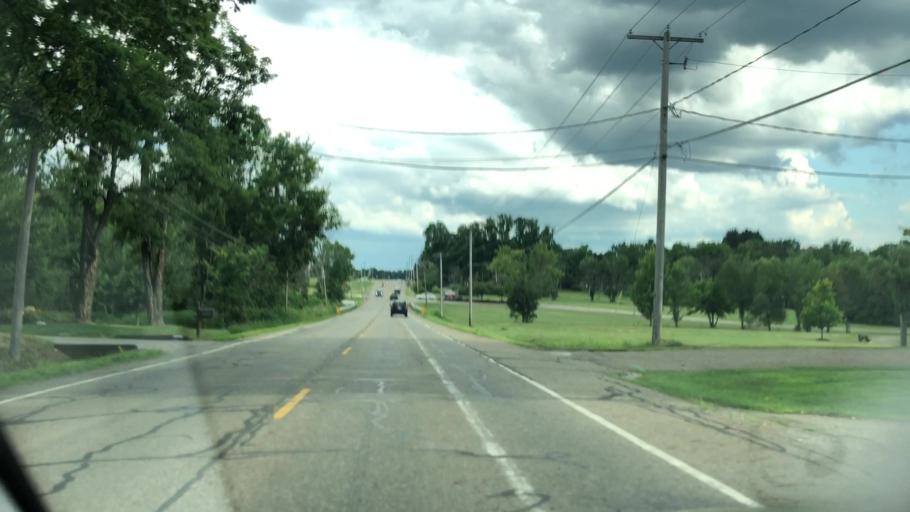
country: US
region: Ohio
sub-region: Summit County
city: Greensburg
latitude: 40.9186
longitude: -81.4626
